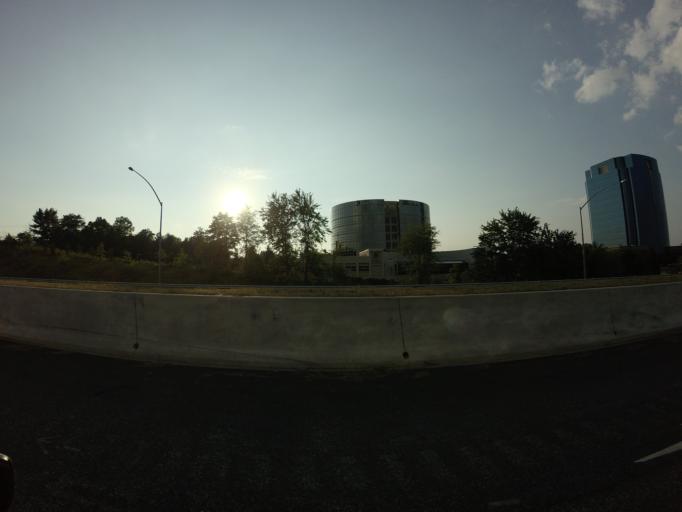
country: US
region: Maryland
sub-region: Prince George's County
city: West Laurel
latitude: 39.0864
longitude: -76.8965
